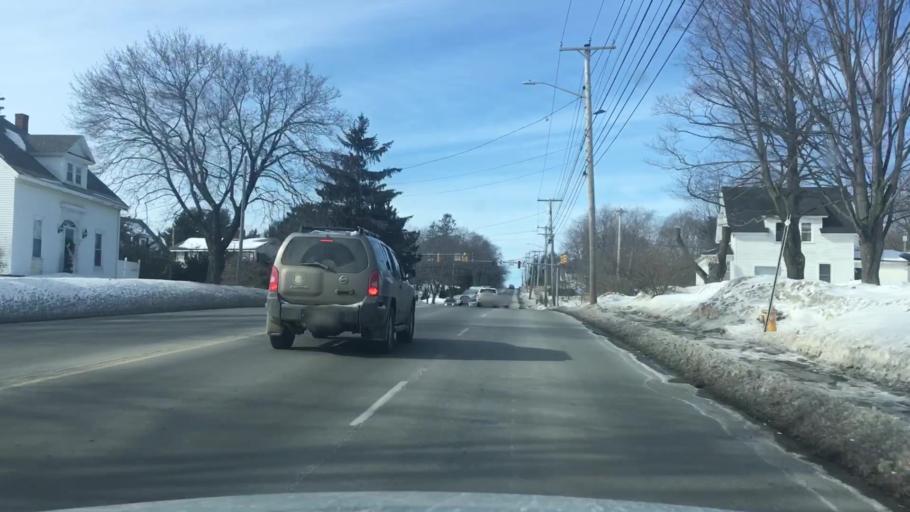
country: US
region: Maine
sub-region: Penobscot County
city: Bangor
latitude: 44.8266
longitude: -68.7822
